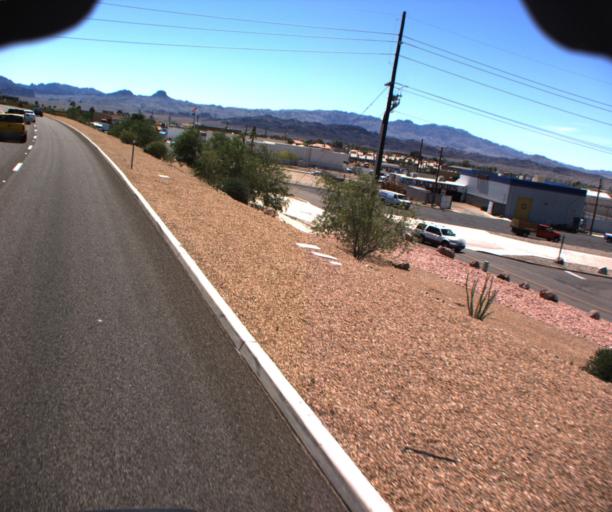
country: US
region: Arizona
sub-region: Mohave County
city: Lake Havasu City
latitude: 34.4781
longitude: -114.3490
